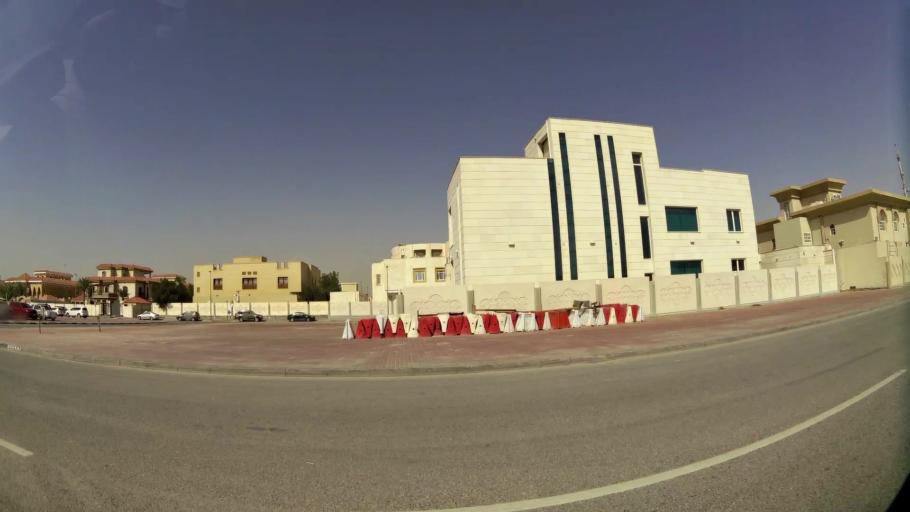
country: QA
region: Baladiyat ad Dawhah
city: Doha
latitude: 25.3549
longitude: 51.5109
